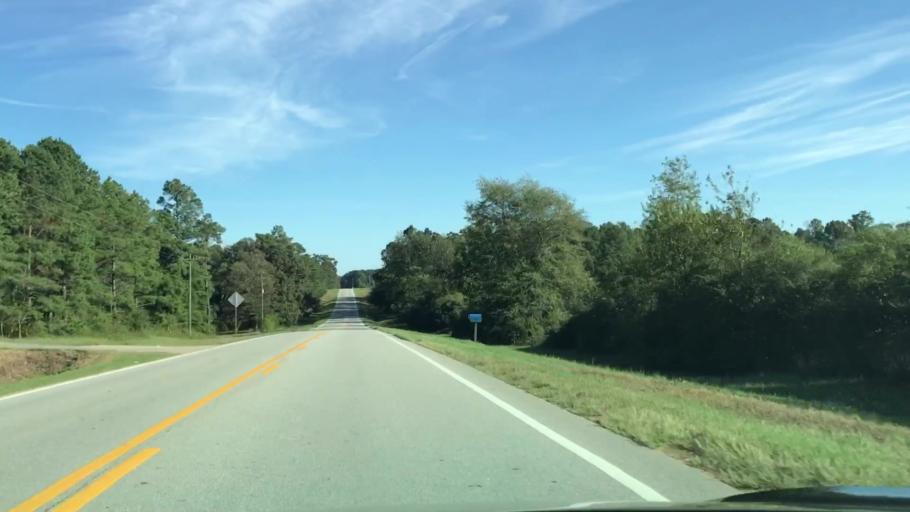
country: US
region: Georgia
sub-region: Glascock County
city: Gibson
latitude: 33.3165
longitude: -82.5464
